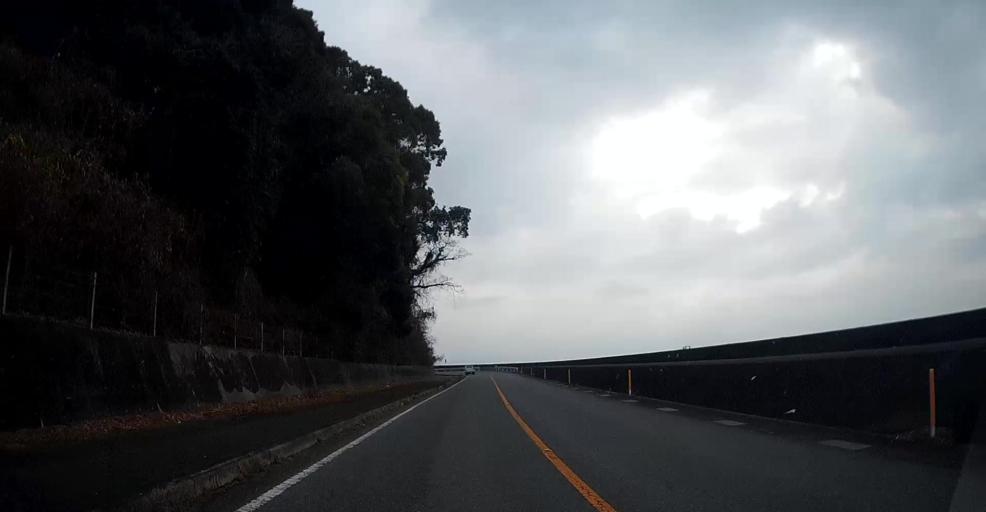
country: JP
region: Kumamoto
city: Matsubase
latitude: 32.6329
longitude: 130.6258
